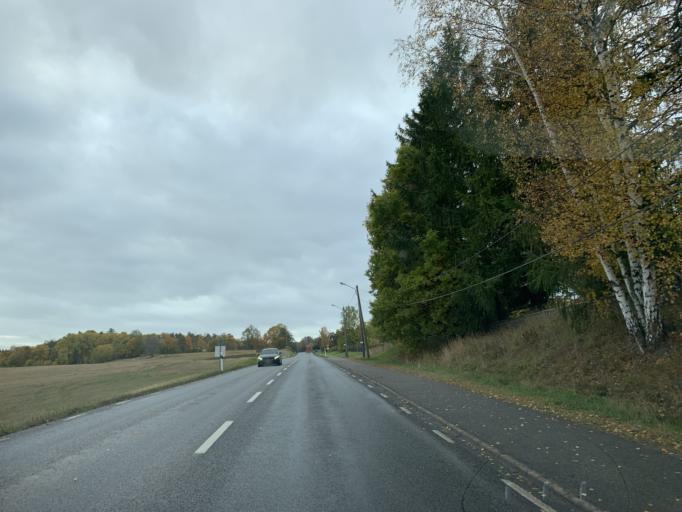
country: SE
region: Stockholm
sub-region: Nynashamns Kommun
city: Osmo
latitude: 59.0067
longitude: 17.8050
